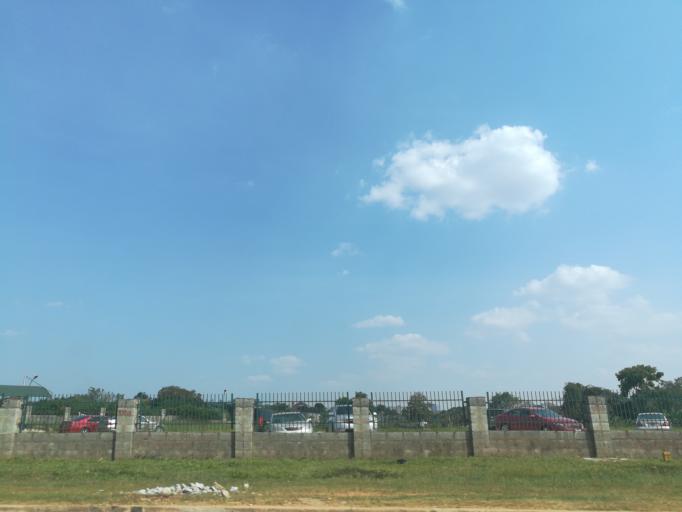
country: NG
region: Abuja Federal Capital Territory
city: Abuja
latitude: 9.0614
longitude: 7.4360
